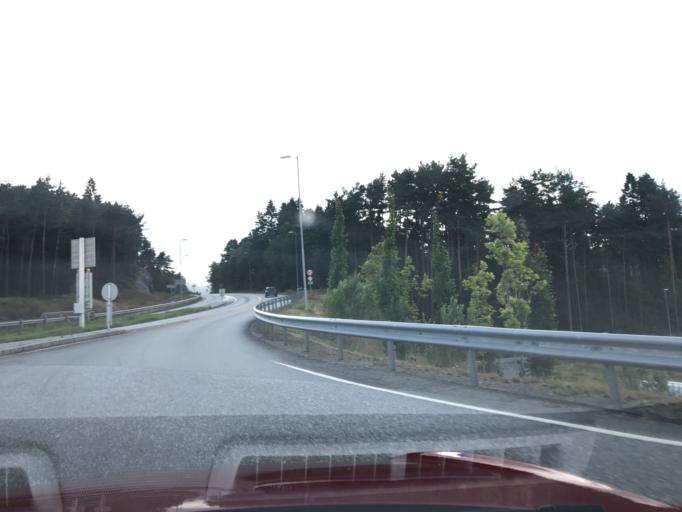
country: NO
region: Hordaland
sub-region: Stord
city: Leirvik
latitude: 59.7750
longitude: 5.4847
